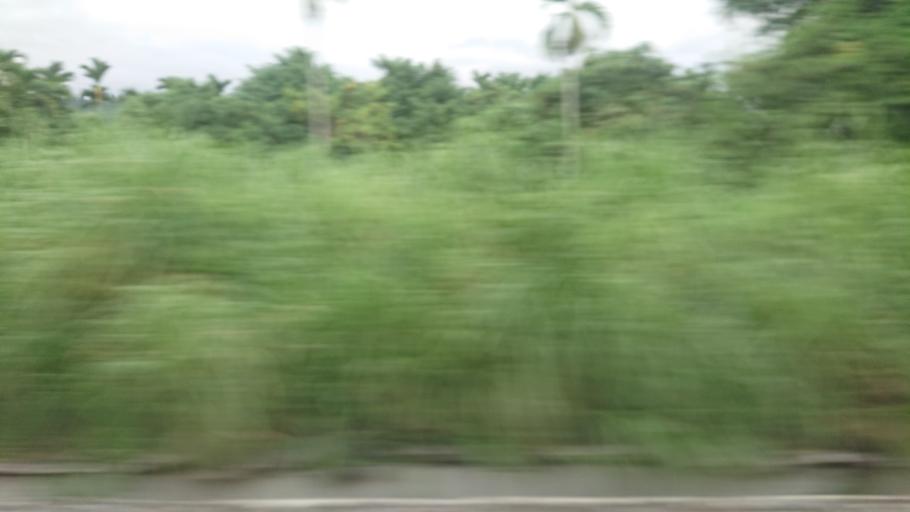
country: TW
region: Taiwan
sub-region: Hualien
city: Hualian
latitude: 23.7911
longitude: 121.4596
